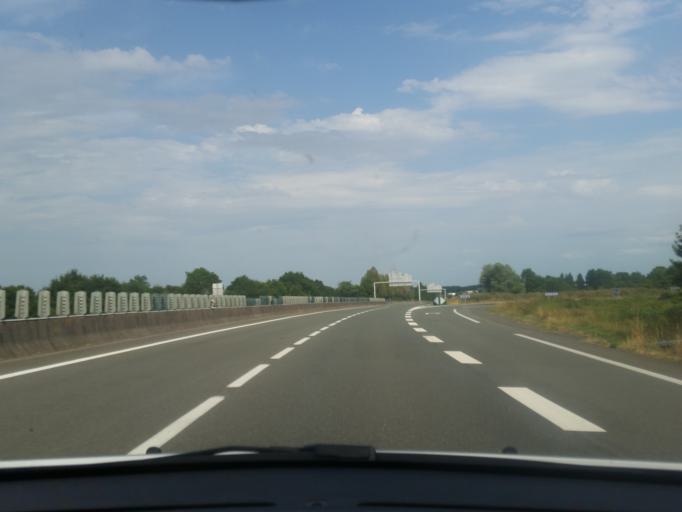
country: FR
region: Pays de la Loire
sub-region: Departement de Maine-et-Loire
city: Saint-Lambert-la-Potherie
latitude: 47.4673
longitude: -0.6783
